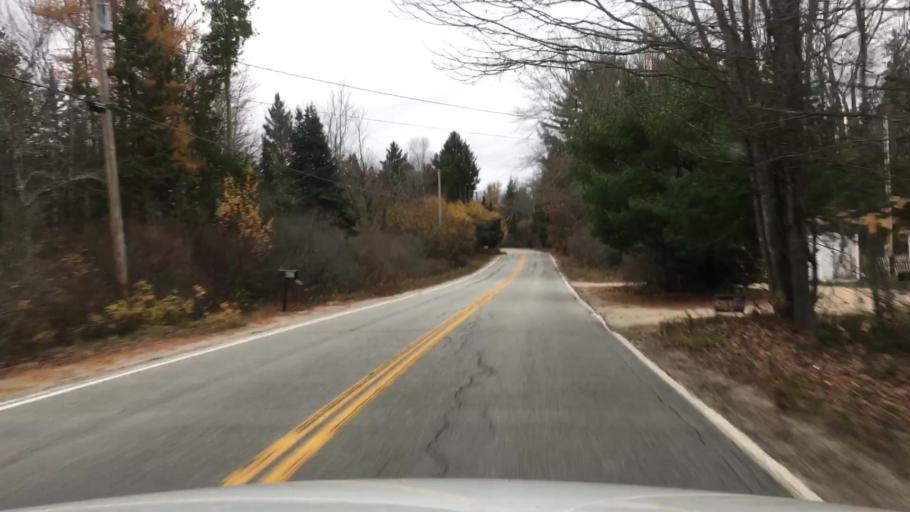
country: US
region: Maine
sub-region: Hancock County
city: Sedgwick
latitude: 44.2896
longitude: -68.5552
